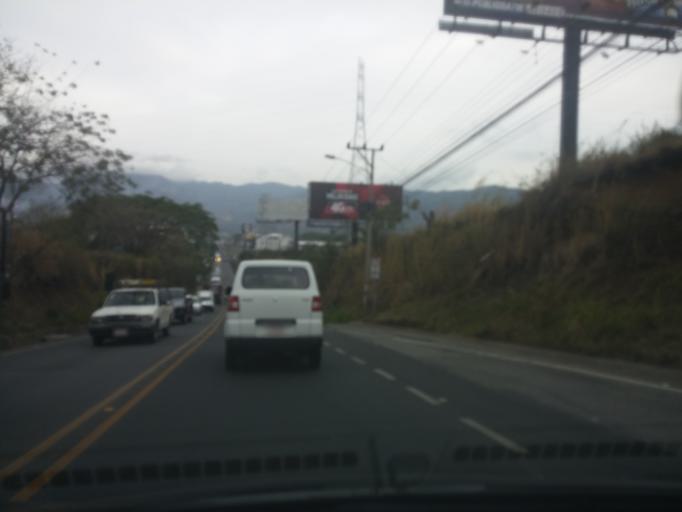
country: CR
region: Heredia
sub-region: Canton de Belen
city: San Antonio
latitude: 9.9678
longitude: -84.1999
